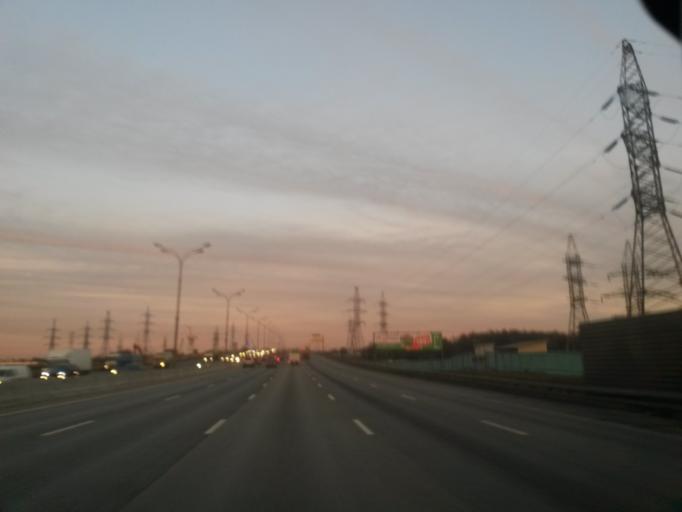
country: RU
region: Moscow
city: Tyoply Stan
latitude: 55.6055
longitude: 37.4988
